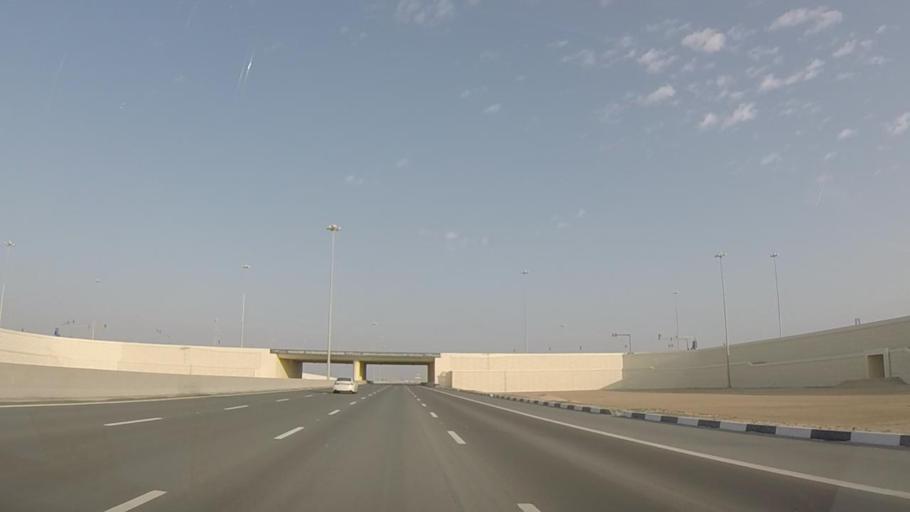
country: AE
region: Abu Dhabi
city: Abu Dhabi
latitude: 24.7344
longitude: 54.7422
